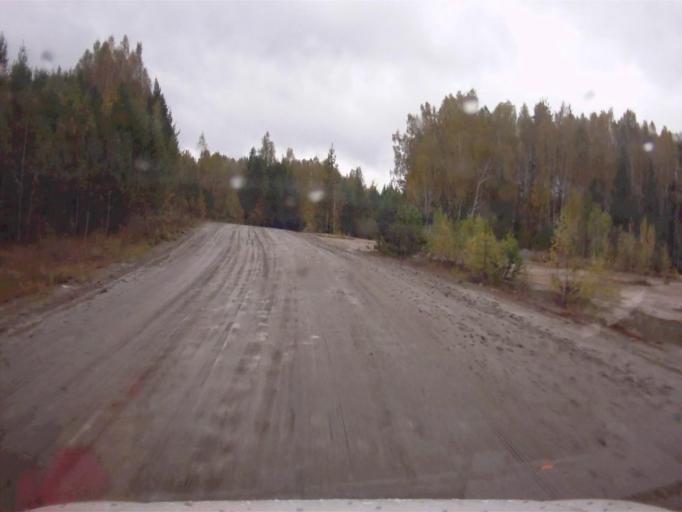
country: RU
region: Chelyabinsk
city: Kyshtym
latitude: 55.8243
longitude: 60.4844
